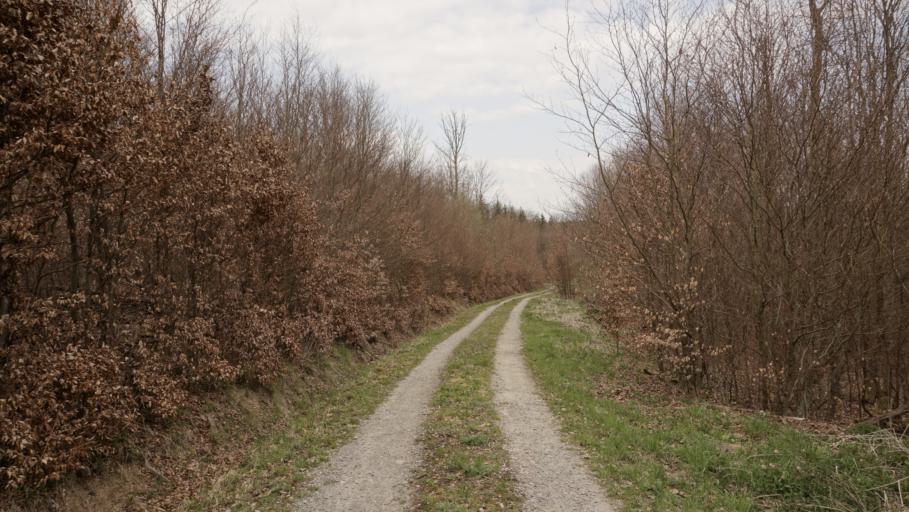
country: DE
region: Baden-Wuerttemberg
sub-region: Karlsruhe Region
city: Mosbach
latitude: 49.3808
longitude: 9.1471
